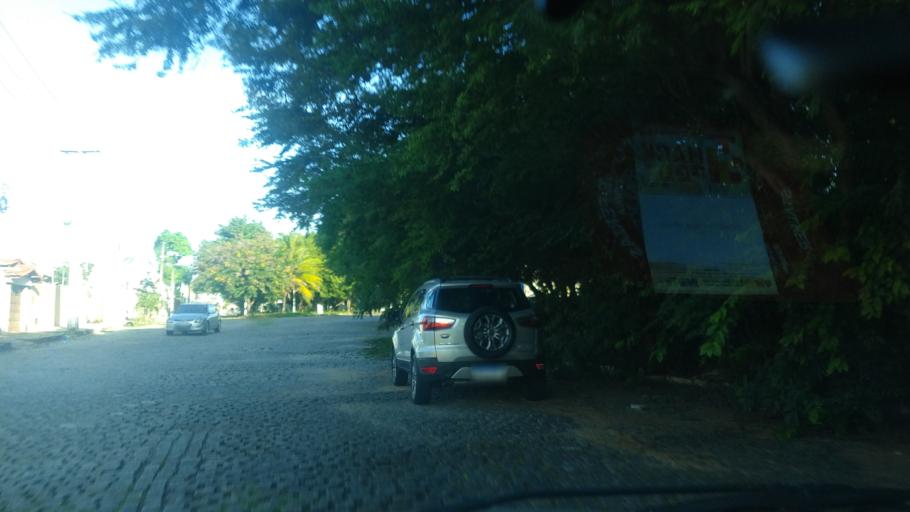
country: BR
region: Rio Grande do Norte
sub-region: Parnamirim
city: Parnamirim
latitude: -5.8789
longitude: -35.1844
